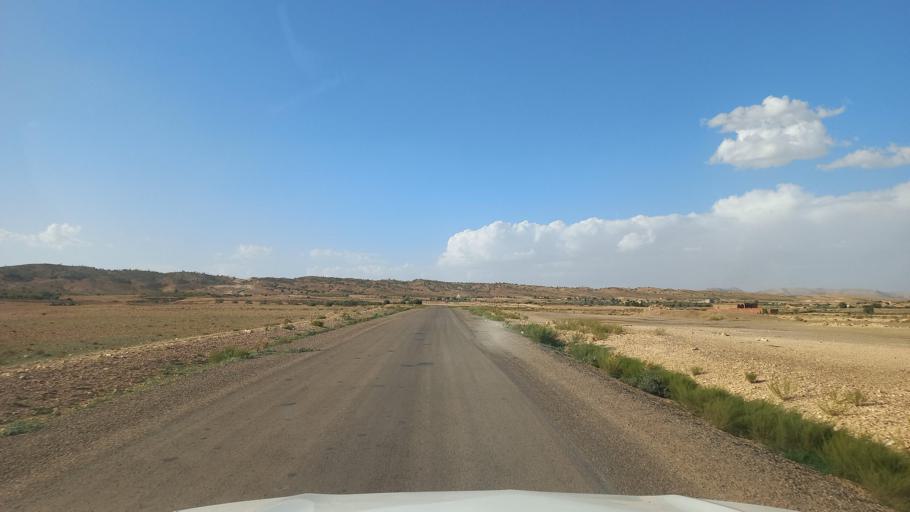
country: TN
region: Al Qasrayn
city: Sbiba
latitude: 35.3456
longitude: 8.9898
